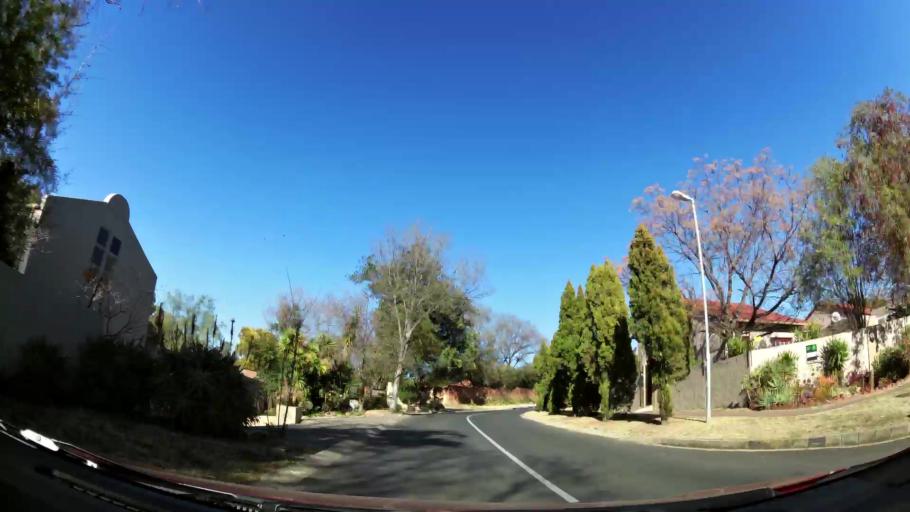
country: ZA
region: Gauteng
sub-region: City of Johannesburg Metropolitan Municipality
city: Diepsloot
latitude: -26.0503
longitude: 27.9874
